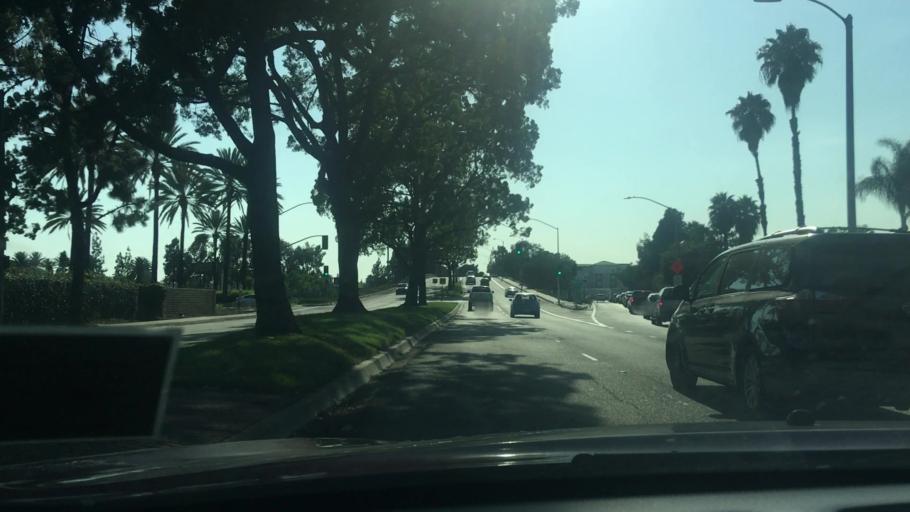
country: US
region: California
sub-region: Los Angeles County
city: Cerritos
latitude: 33.8733
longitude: -118.0571
